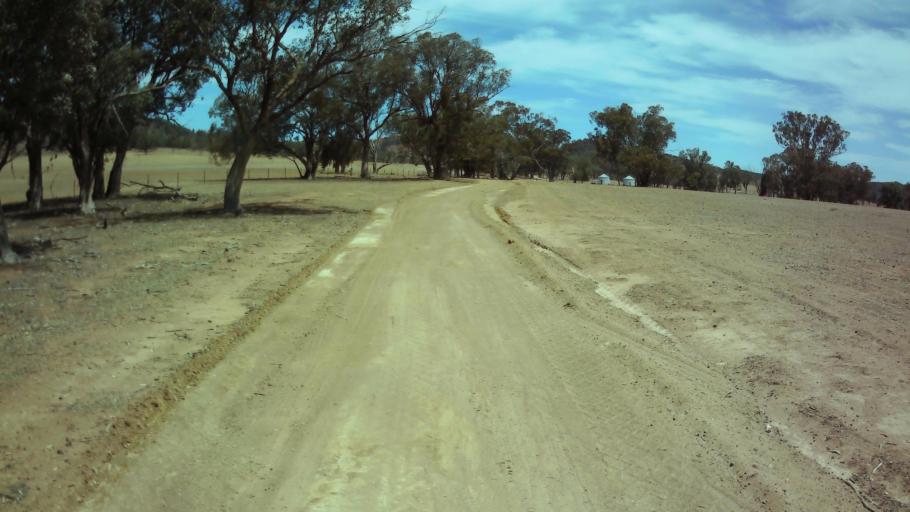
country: AU
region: New South Wales
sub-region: Weddin
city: Grenfell
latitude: -33.7744
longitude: 148.1519
